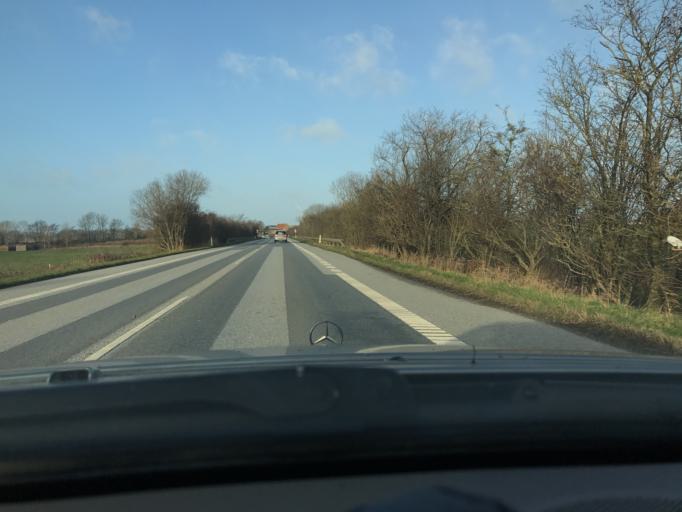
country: DK
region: South Denmark
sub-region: Sonderborg Kommune
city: Horuphav
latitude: 54.8919
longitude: 9.9714
